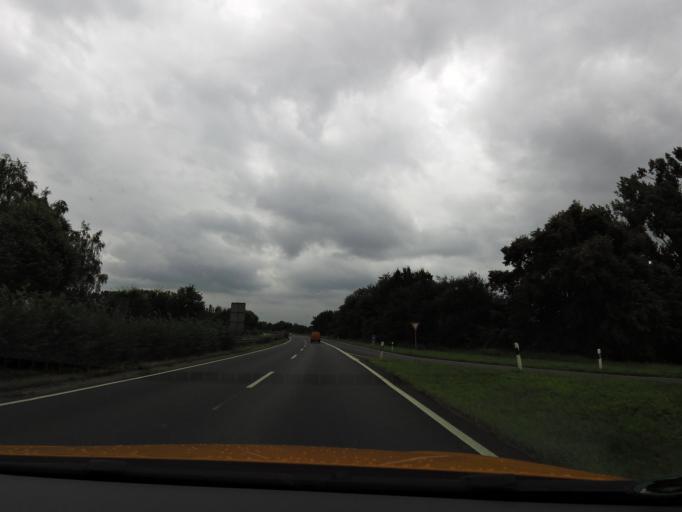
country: DE
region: Lower Saxony
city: Neustadt am Rubenberge
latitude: 52.5010
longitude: 9.4740
